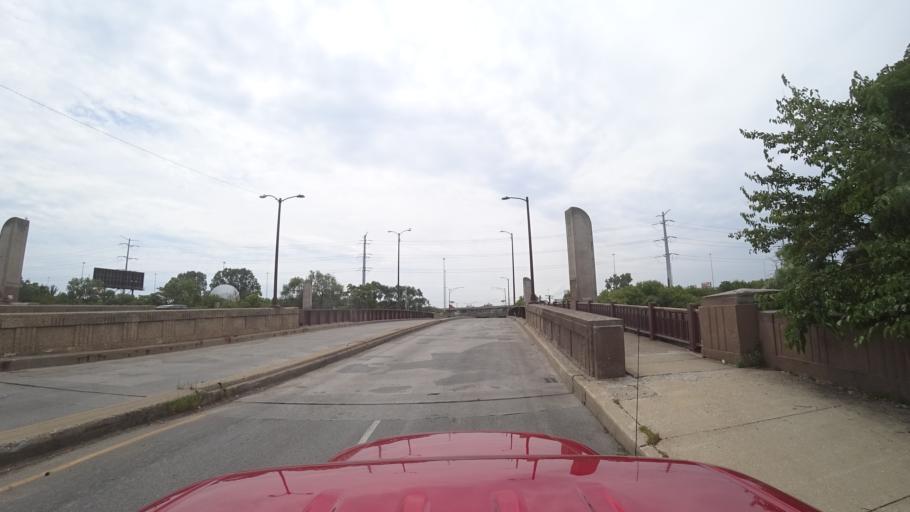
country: US
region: Illinois
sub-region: Cook County
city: Chicago
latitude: 41.8382
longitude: -87.6854
